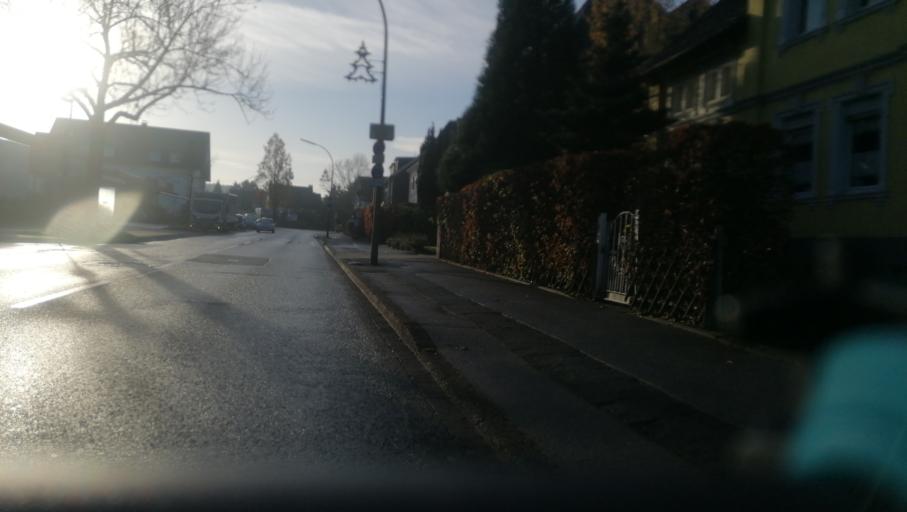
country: DE
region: North Rhine-Westphalia
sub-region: Regierungsbezirk Arnsberg
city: Dortmund
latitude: 51.4660
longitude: 7.4937
